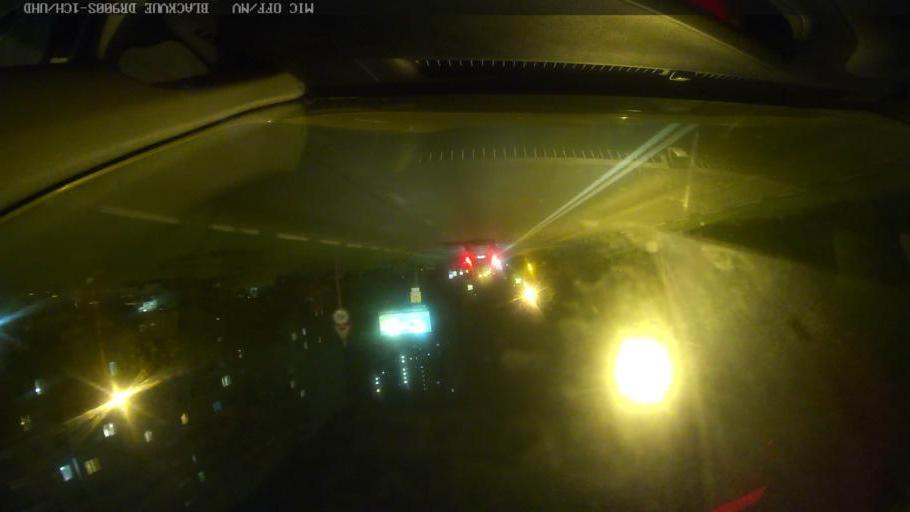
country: RU
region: Moskovskaya
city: Reutov
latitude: 55.7483
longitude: 37.8564
